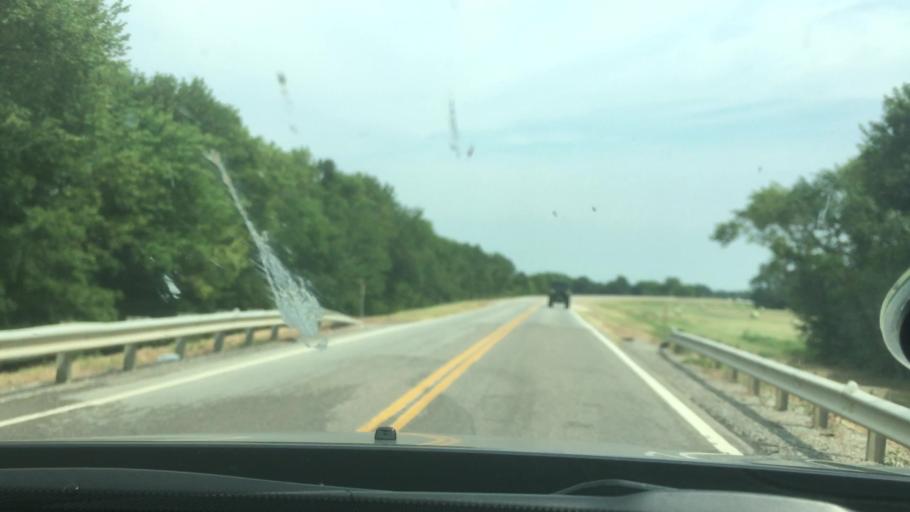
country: US
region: Oklahoma
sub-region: Coal County
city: Coalgate
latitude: 34.5372
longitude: -96.4077
